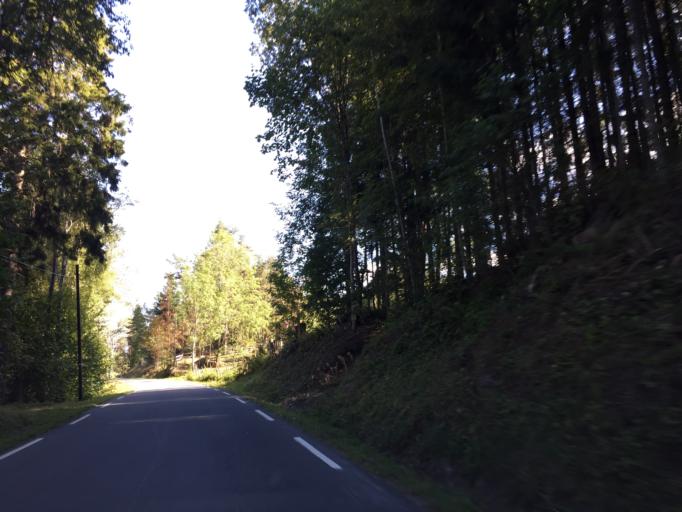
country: NO
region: Buskerud
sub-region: Ovre Eiker
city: Hokksund
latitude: 59.6781
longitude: 9.8637
